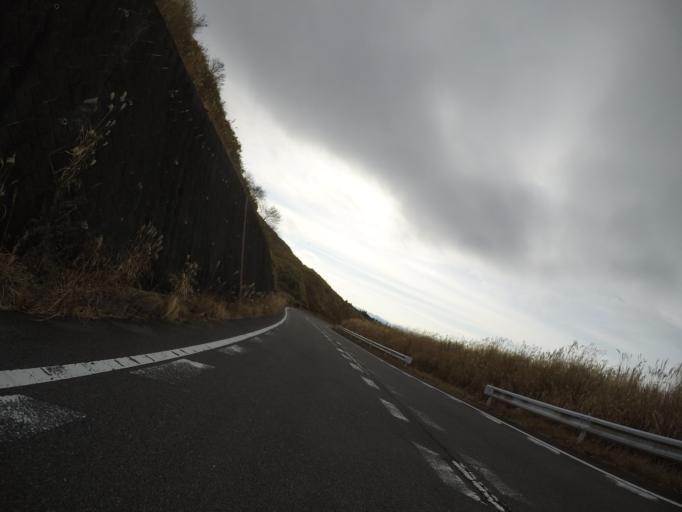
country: JP
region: Shizuoka
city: Heda
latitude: 34.8579
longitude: 138.8452
